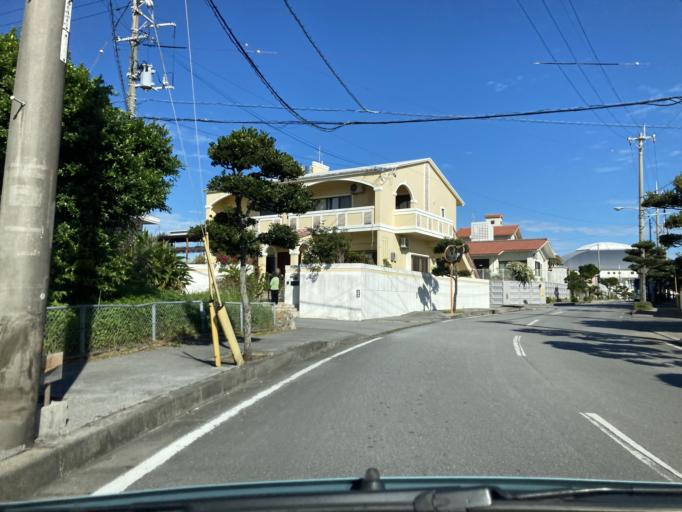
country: JP
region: Okinawa
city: Okinawa
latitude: 26.3669
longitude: 127.7722
